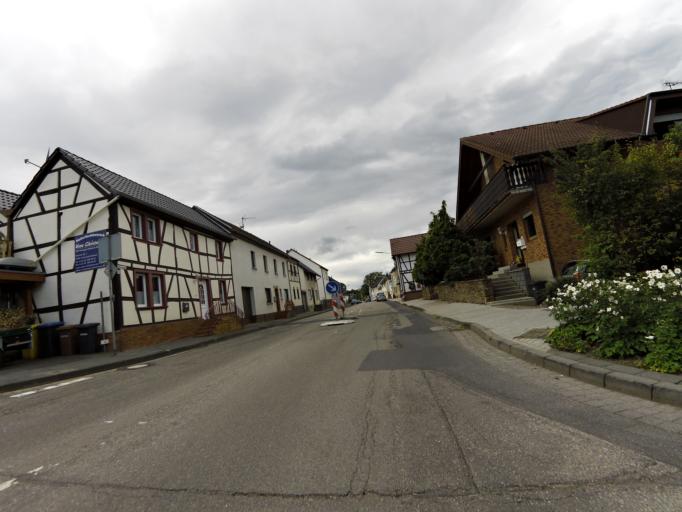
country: DE
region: North Rhine-Westphalia
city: Meckenheim
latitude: 50.5831
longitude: 7.0329
